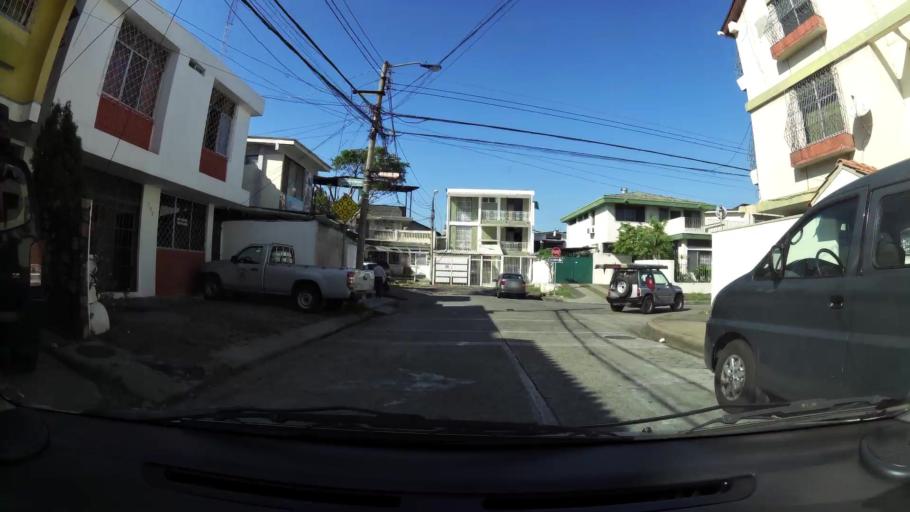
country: EC
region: Guayas
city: Guayaquil
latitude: -2.1760
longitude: -79.8958
